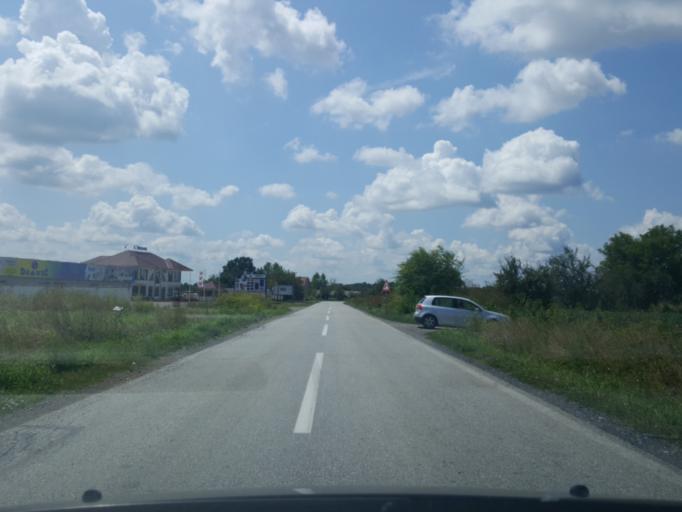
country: RS
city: Metkovic
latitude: 44.8434
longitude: 19.5176
